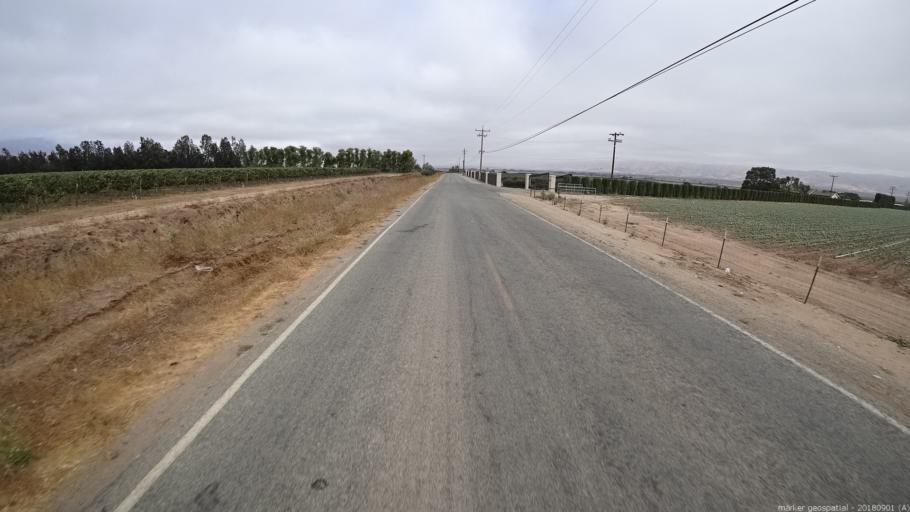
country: US
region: California
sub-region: Monterey County
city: Soledad
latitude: 36.3668
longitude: -121.3236
